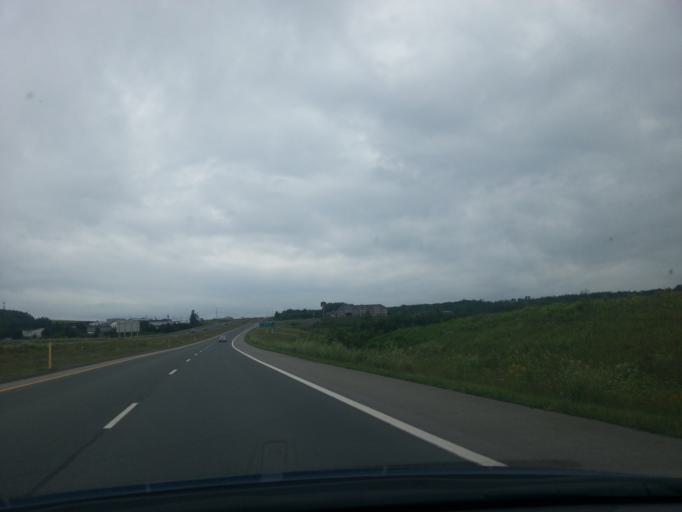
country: US
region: Maine
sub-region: Aroostook County
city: Limestone
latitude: 47.0502
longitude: -67.7653
